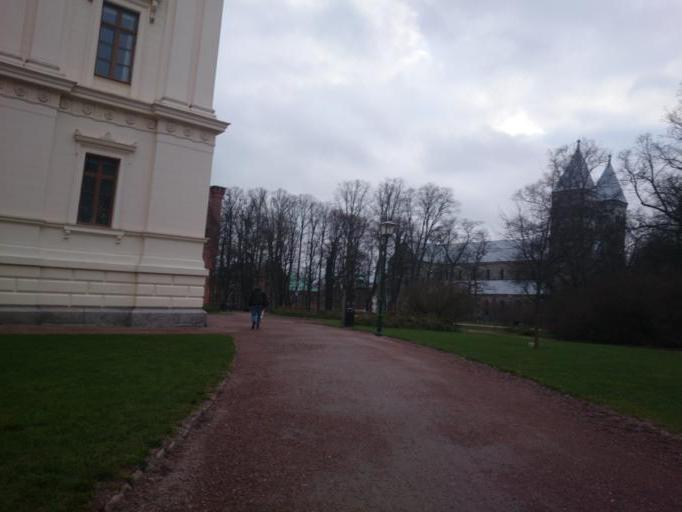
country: SE
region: Skane
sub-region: Lunds Kommun
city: Lund
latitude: 55.7057
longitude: 13.1923
